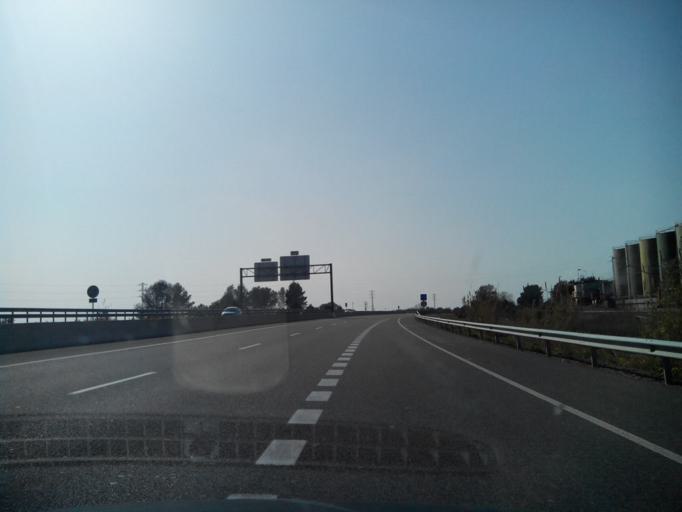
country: ES
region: Catalonia
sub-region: Provincia de Tarragona
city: Alcover
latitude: 41.2501
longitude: 1.1727
